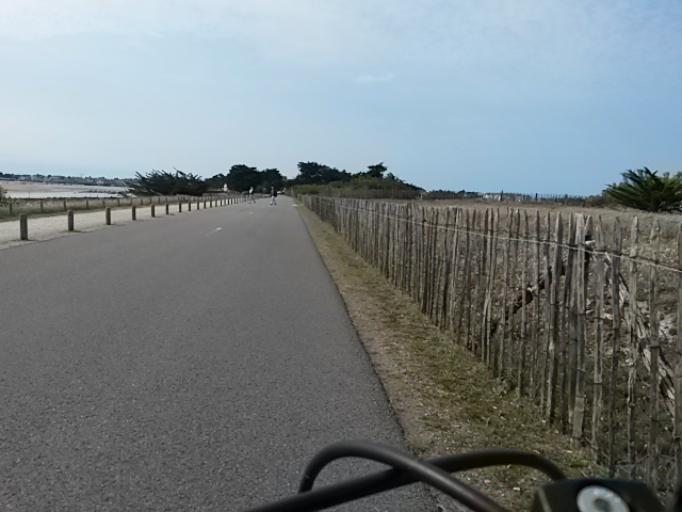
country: FR
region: Pays de la Loire
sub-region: Departement de la Loire-Atlantique
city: Le Croisic
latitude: 47.3092
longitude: -2.5071
